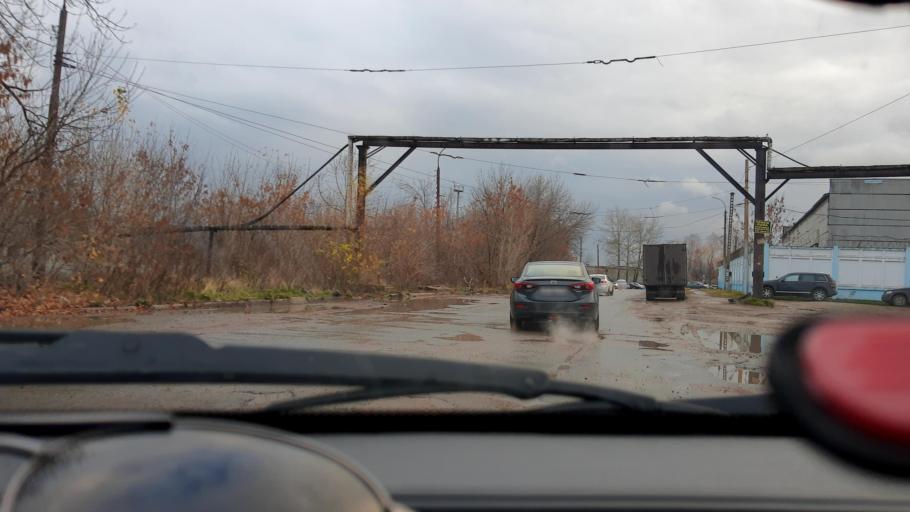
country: RU
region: Bashkortostan
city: Ufa
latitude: 54.8325
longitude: 56.1178
